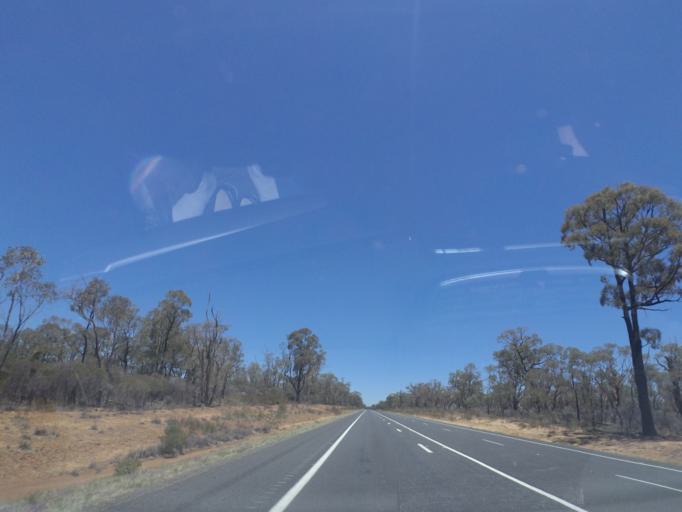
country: AU
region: New South Wales
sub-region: Warrumbungle Shire
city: Coonabarabran
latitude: -30.8711
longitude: 149.4501
